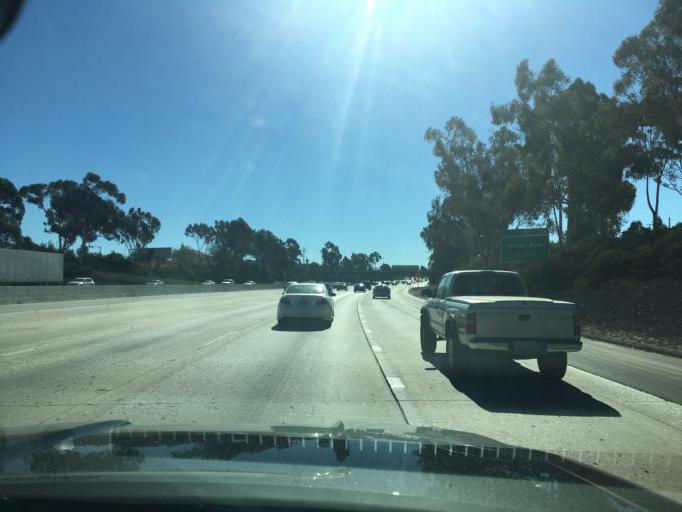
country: US
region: California
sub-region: San Diego County
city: National City
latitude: 32.7038
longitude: -117.0951
